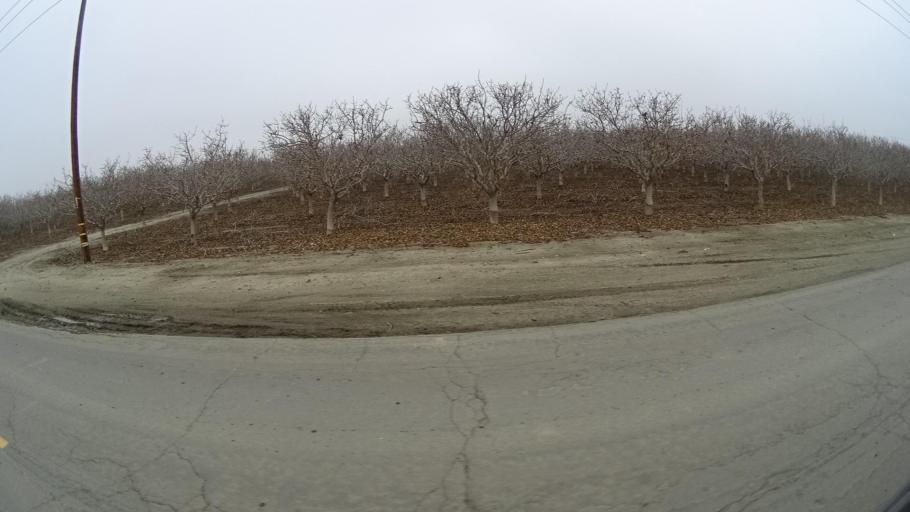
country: US
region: California
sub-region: Kern County
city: Wasco
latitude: 35.7175
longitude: -119.4415
